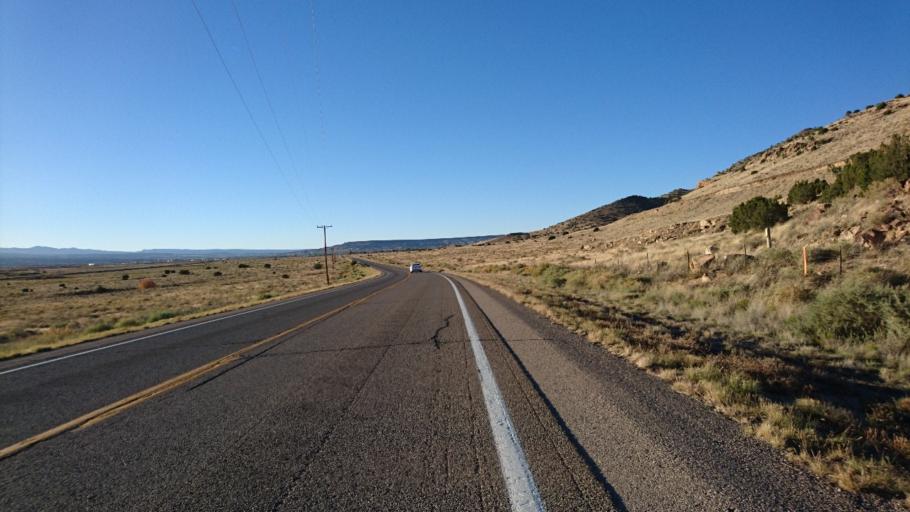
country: US
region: New Mexico
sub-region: Cibola County
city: Grants
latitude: 35.1139
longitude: -107.7843
